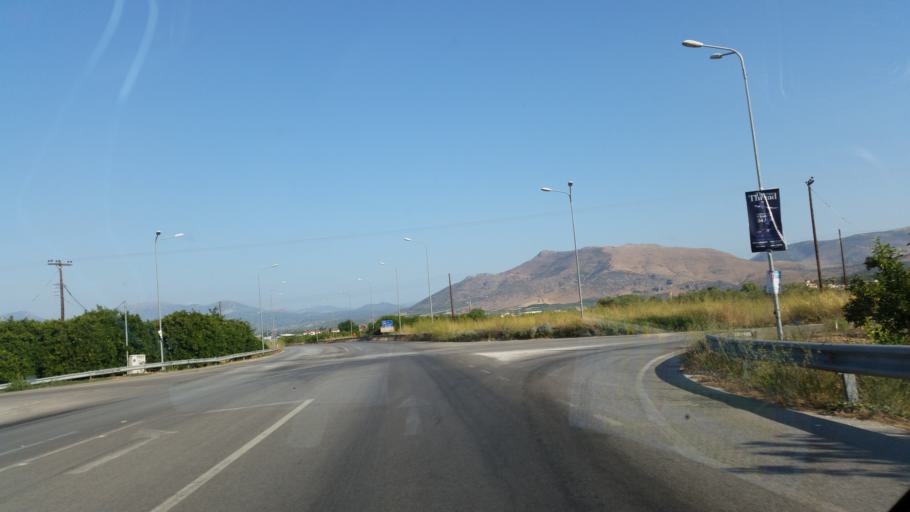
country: GR
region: Peloponnese
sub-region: Nomos Argolidos
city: Ayia Trias
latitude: 37.6402
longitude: 22.8158
